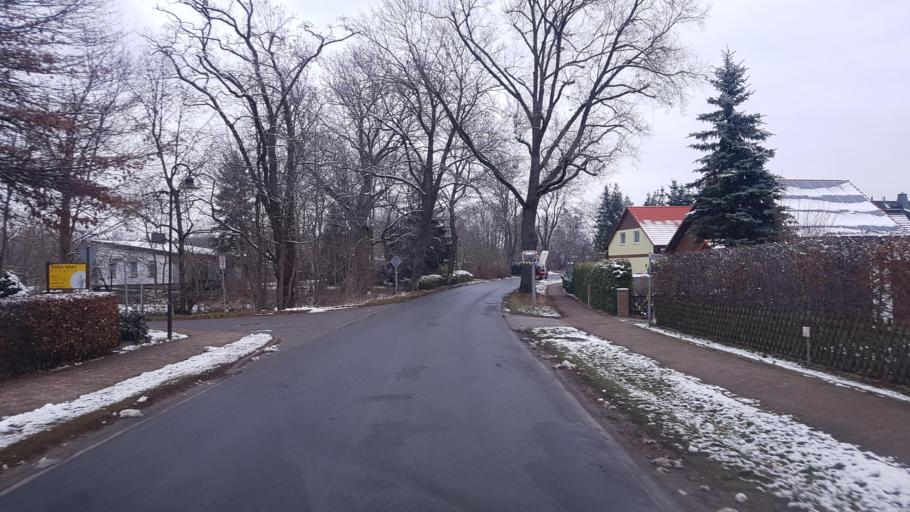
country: DE
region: Brandenburg
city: Rehfelde
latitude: 52.5312
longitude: 13.9277
